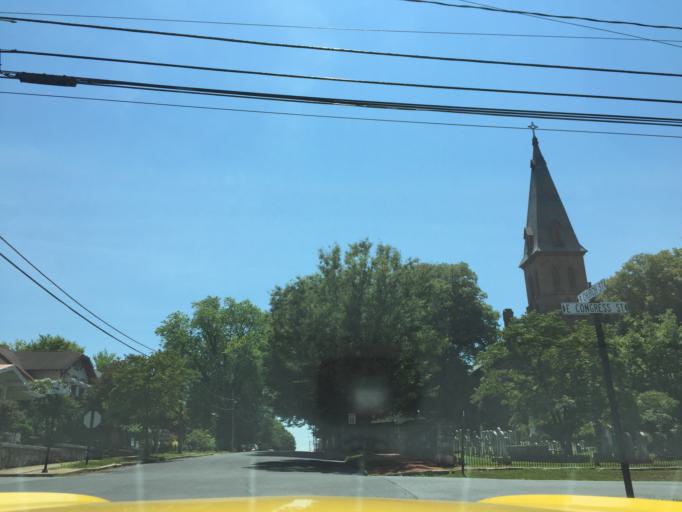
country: US
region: West Virginia
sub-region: Jefferson County
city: Charles Town
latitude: 39.2897
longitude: -77.8559
